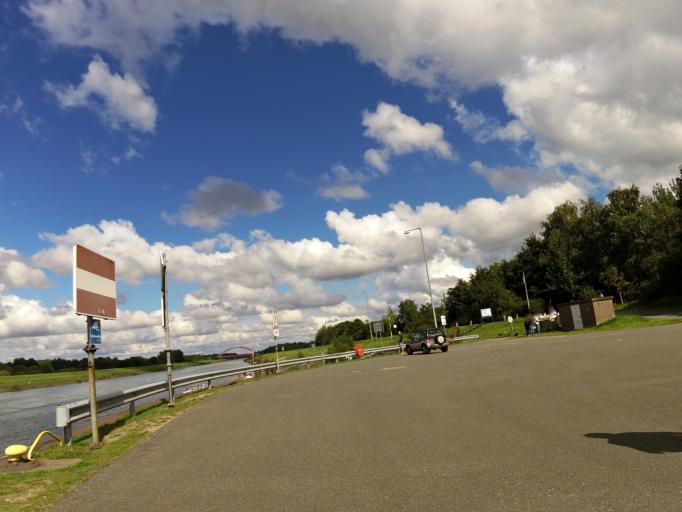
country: DE
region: Lower Saxony
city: Scharnebeck
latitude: 53.2979
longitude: 10.4900
